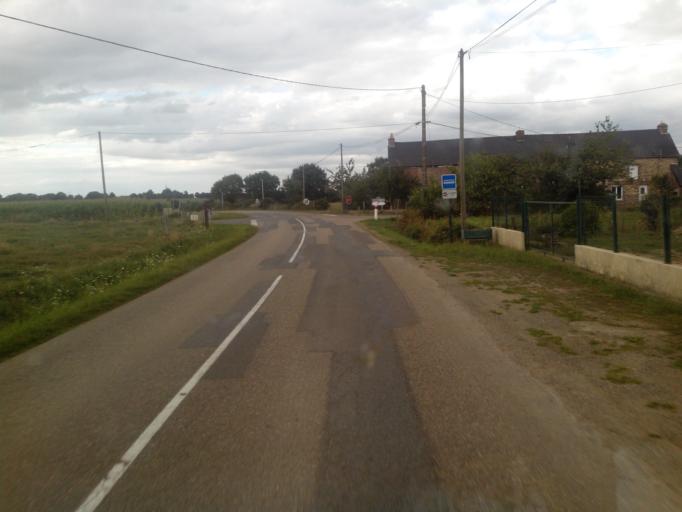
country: FR
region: Brittany
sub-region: Departement d'Ille-et-Vilaine
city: Maxent
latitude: 47.9662
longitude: -2.0162
